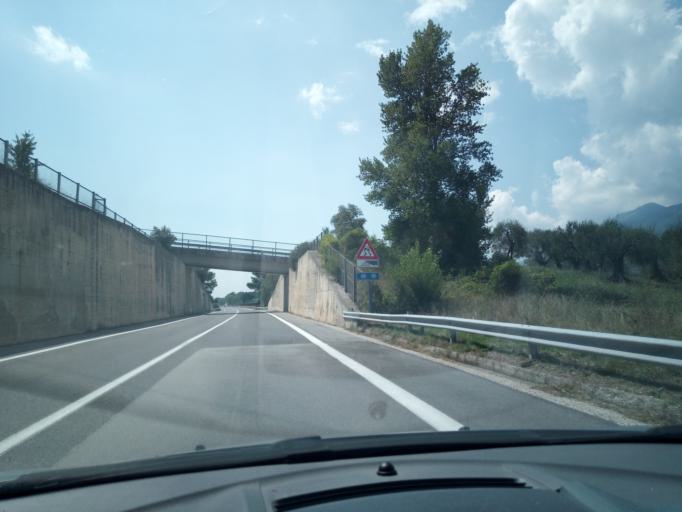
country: IT
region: Campania
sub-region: Provincia di Avellino
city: Calabritto
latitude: 40.7749
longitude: 15.2425
